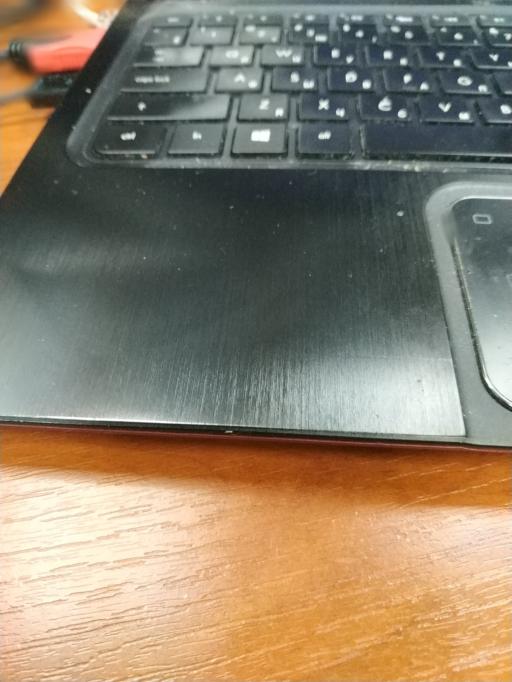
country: RU
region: Moscow
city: Severnyy
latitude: 55.9441
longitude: 37.5606
